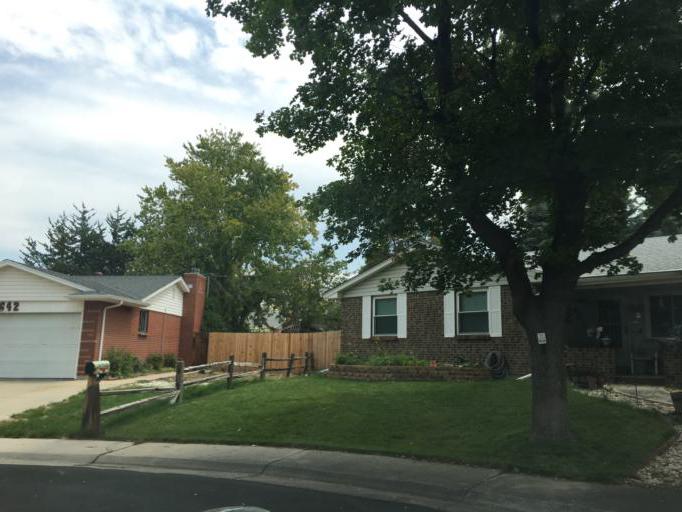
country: US
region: Colorado
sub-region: Adams County
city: Aurora
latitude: 39.7261
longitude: -104.8037
